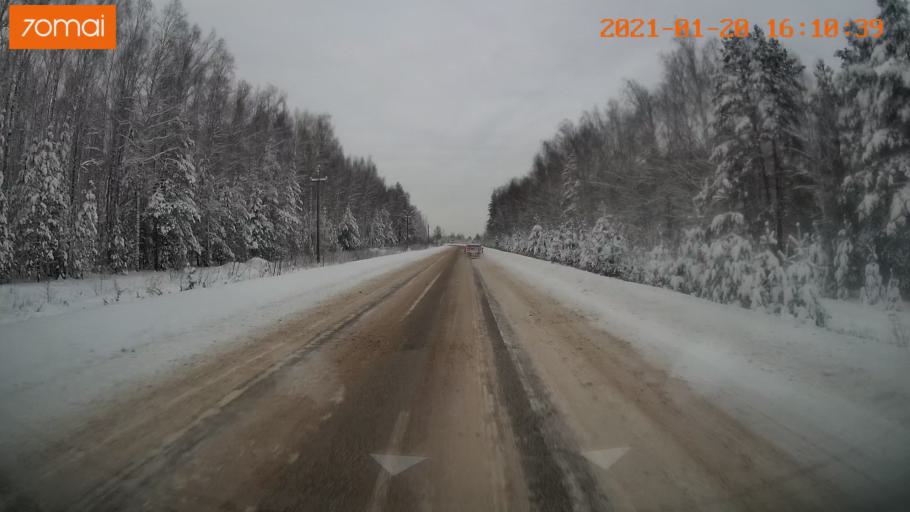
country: RU
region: Vladimir
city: Sudogda
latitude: 56.0941
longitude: 40.7860
